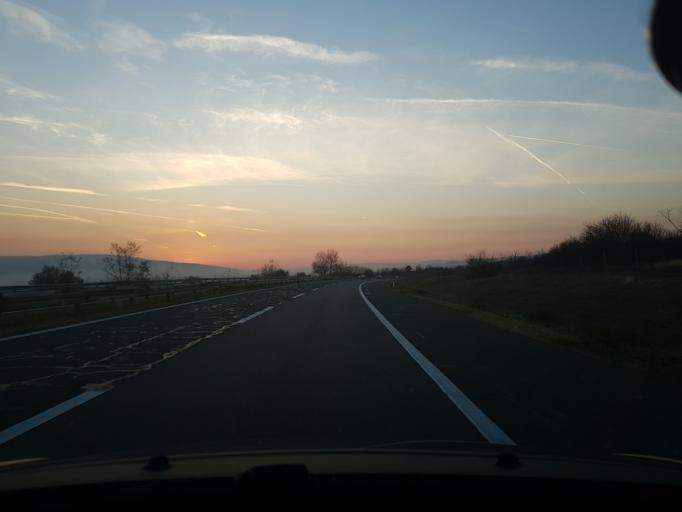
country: RS
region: Central Serbia
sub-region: Nisavski Okrug
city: Razanj
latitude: 43.6212
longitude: 21.5772
